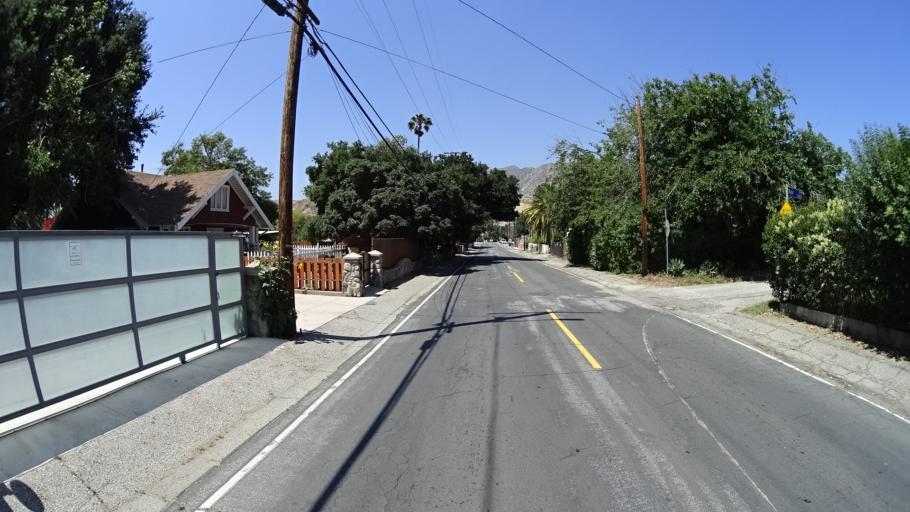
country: US
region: California
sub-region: Los Angeles County
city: Burbank
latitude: 34.2648
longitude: -118.3158
